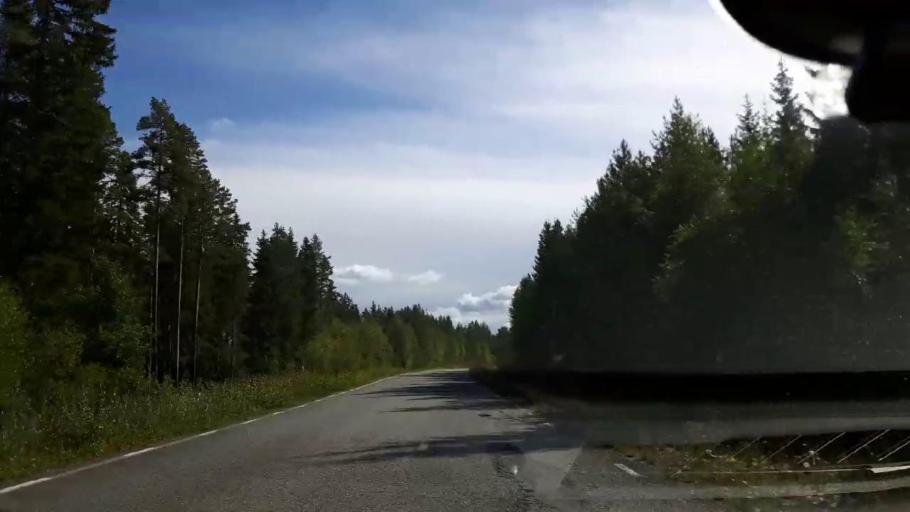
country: SE
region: Jaemtland
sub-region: Braecke Kommun
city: Braecke
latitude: 63.2034
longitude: 15.3594
